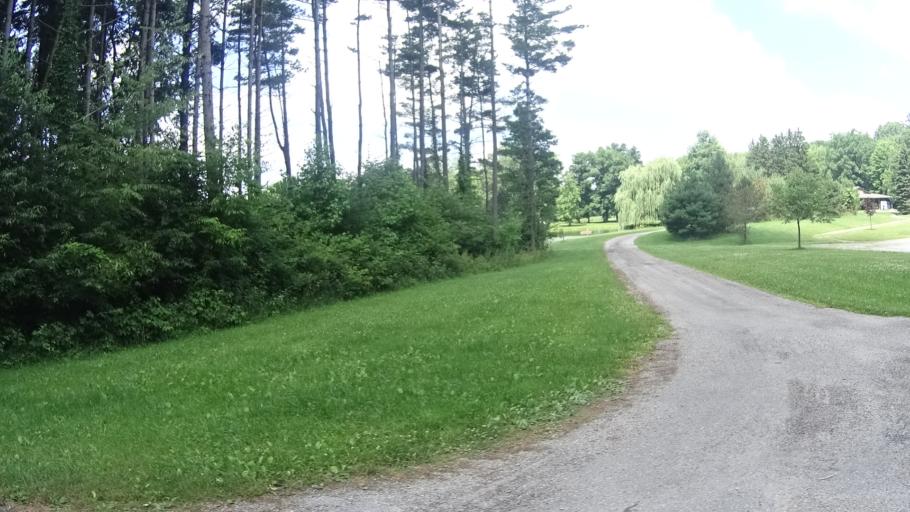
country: US
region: Ohio
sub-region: Lorain County
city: Camden
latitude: 41.2955
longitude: -82.3431
